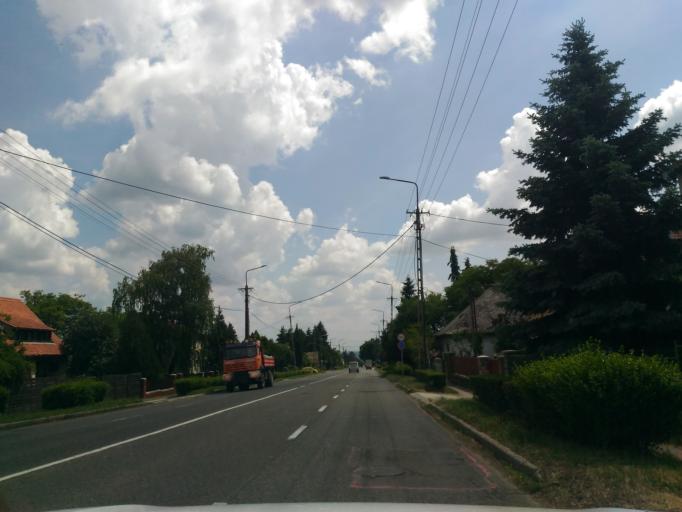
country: HU
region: Baranya
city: Pecs
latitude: 46.1092
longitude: 18.2628
